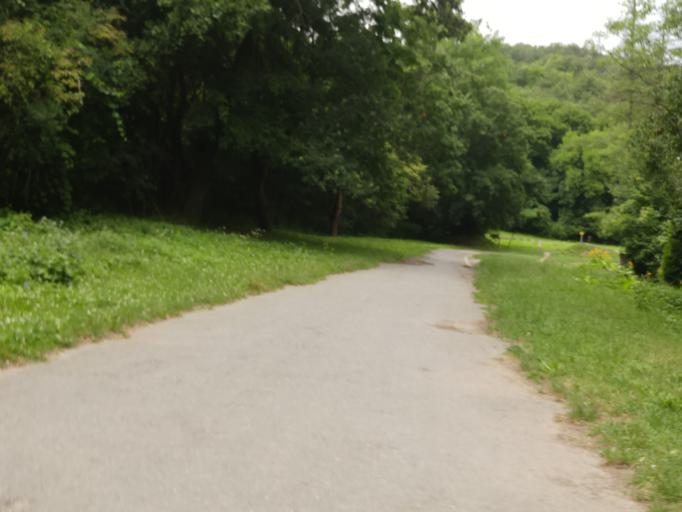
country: CZ
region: Central Bohemia
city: Roztoky
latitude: 50.1520
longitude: 14.3859
